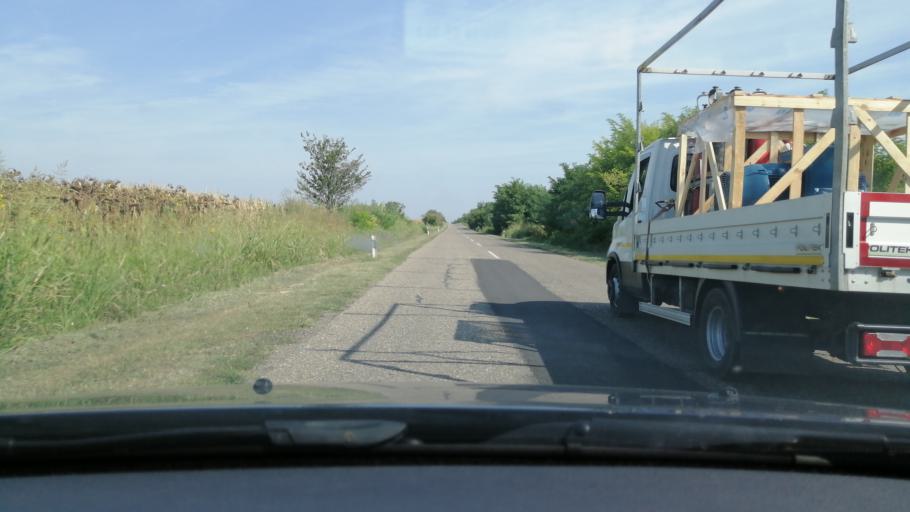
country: RS
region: Autonomna Pokrajina Vojvodina
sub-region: Juznobanatski Okrug
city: Kovacica
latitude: 45.1327
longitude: 20.6160
